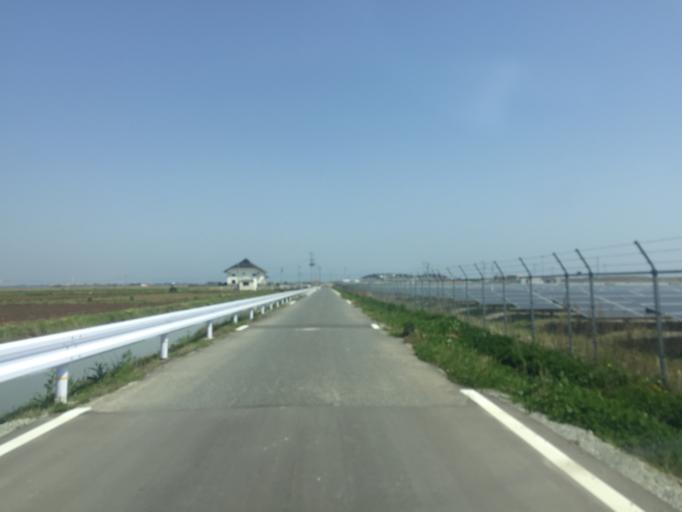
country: JP
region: Miyagi
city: Marumori
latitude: 37.7718
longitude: 140.9775
